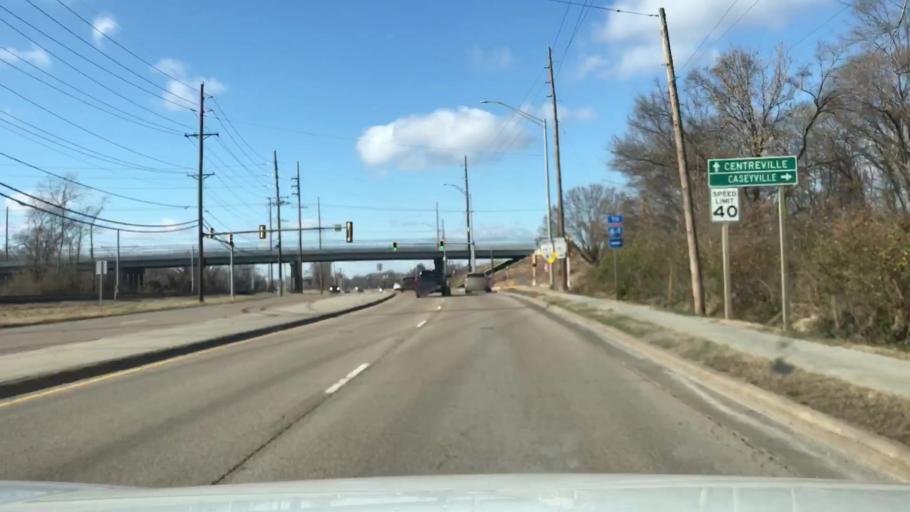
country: US
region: Illinois
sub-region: Saint Clair County
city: Caseyville
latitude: 38.5980
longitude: -90.0512
